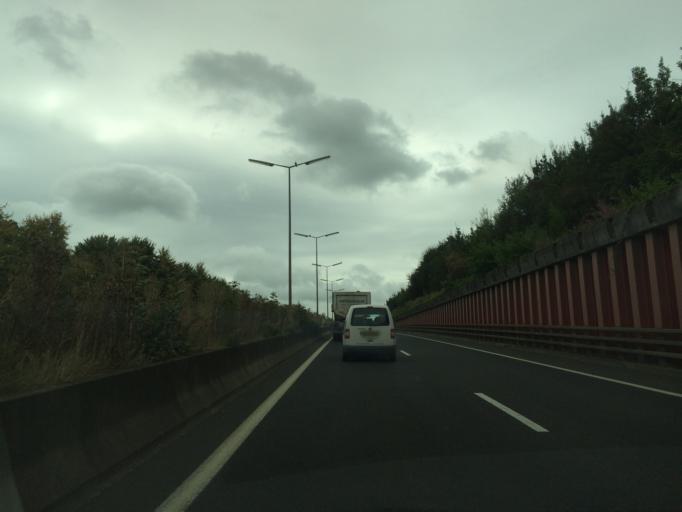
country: LU
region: Luxembourg
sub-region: Canton d'Esch-sur-Alzette
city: Mondercange
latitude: 49.5228
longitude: 5.9692
